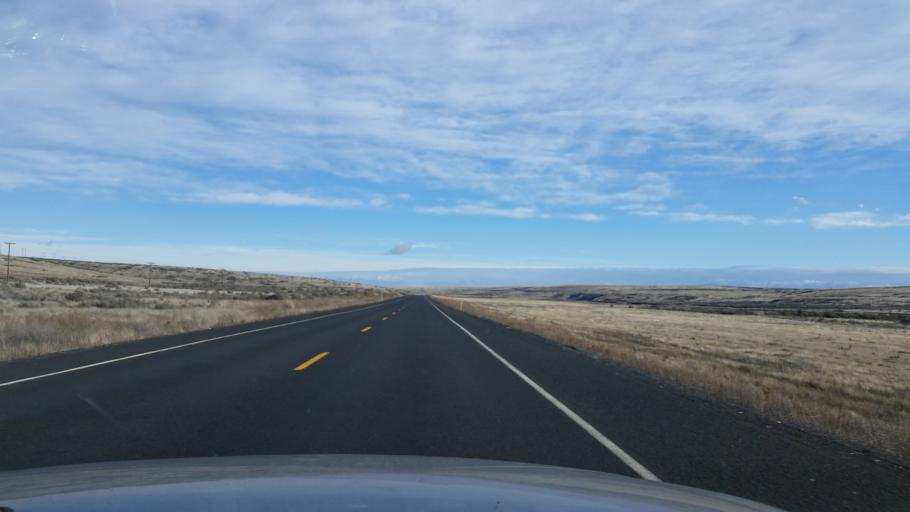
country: US
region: Washington
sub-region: Adams County
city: Ritzville
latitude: 47.3477
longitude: -118.5838
